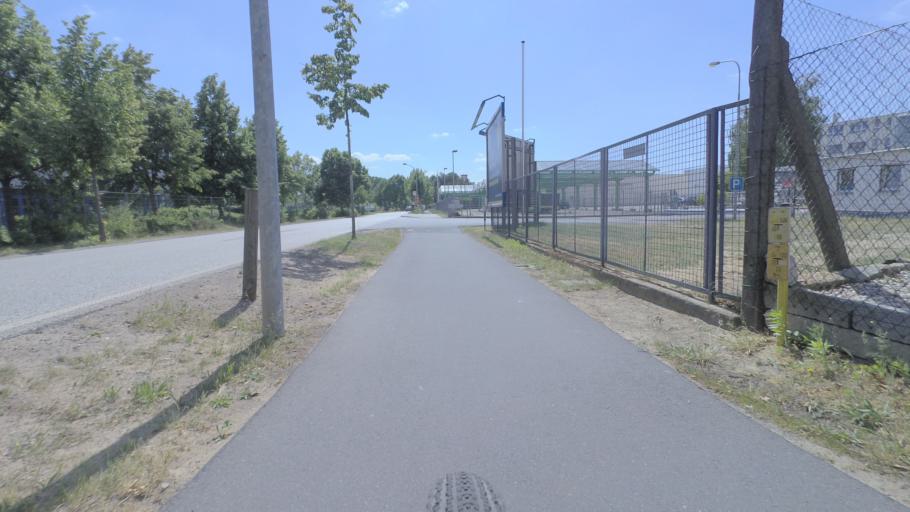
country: DE
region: Brandenburg
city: Ludwigsfelde
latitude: 52.3005
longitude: 13.2743
